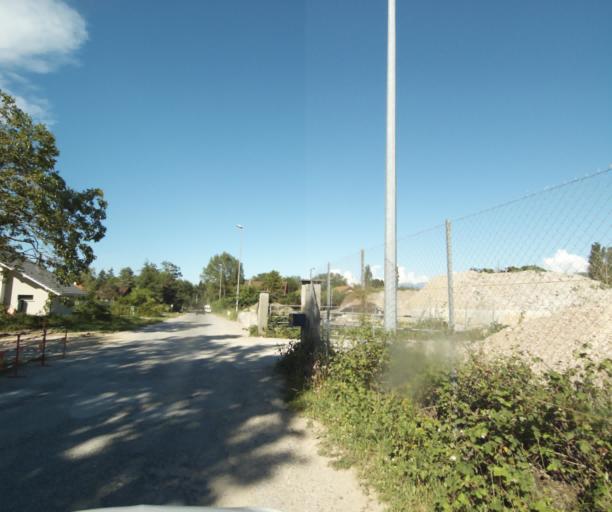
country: FR
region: Rhone-Alpes
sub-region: Departement de la Haute-Savoie
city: Sciez
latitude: 46.3407
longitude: 6.3545
